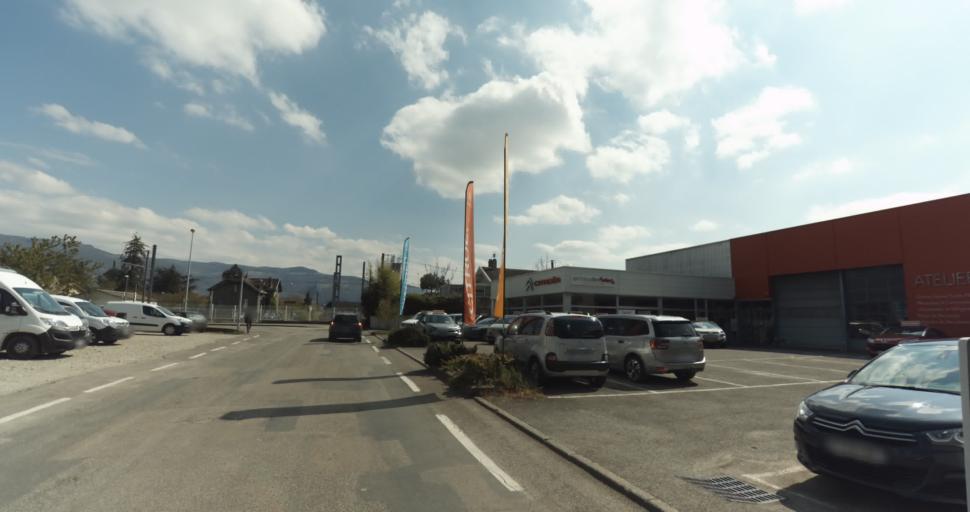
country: FR
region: Rhone-Alpes
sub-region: Departement de l'Isere
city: Saint-Marcellin
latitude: 45.1499
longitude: 5.3204
